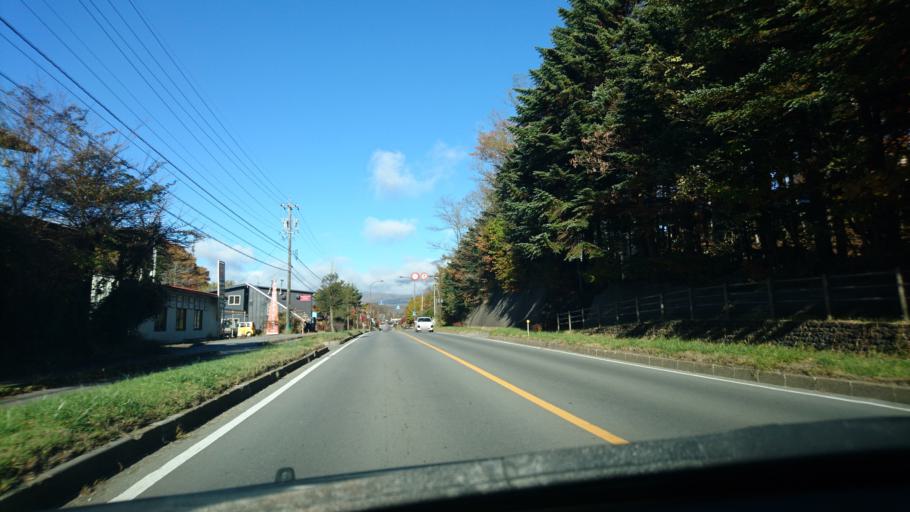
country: JP
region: Nagano
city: Saku
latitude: 36.3308
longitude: 138.6092
